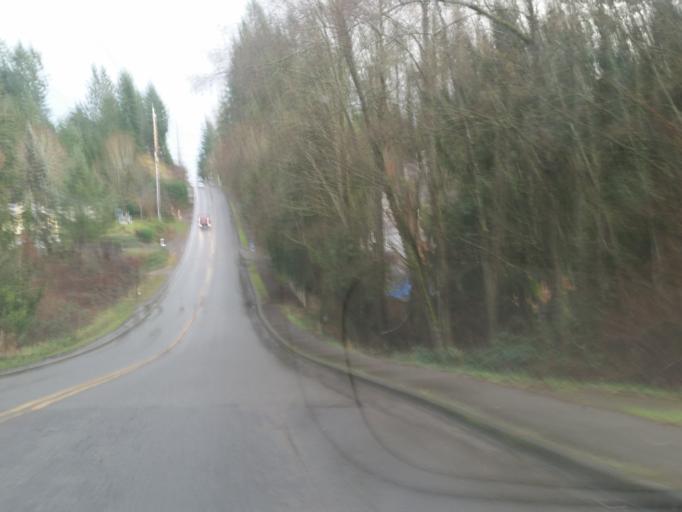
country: US
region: Washington
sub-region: Snohomish County
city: Brier
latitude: 47.7918
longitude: -122.2842
